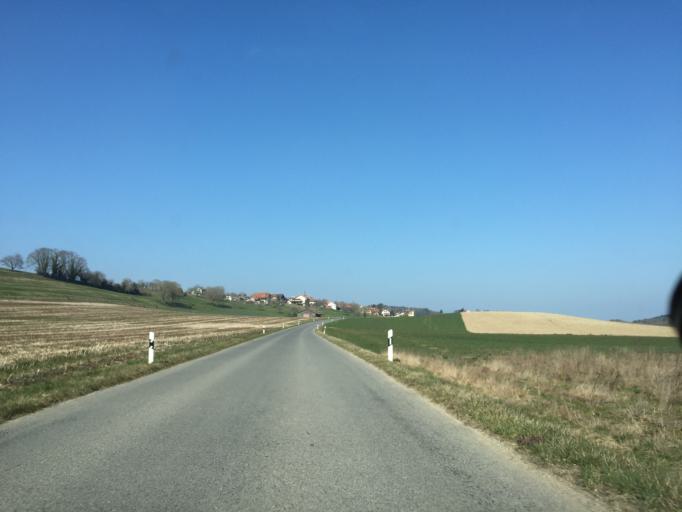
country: CH
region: Vaud
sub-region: Morges District
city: Chevilly
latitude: 46.6354
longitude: 6.4751
